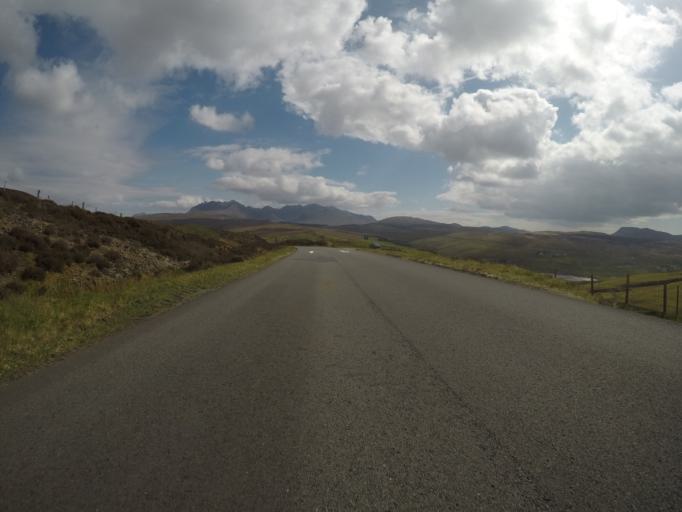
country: GB
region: Scotland
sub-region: Highland
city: Isle of Skye
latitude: 57.3067
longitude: -6.3152
